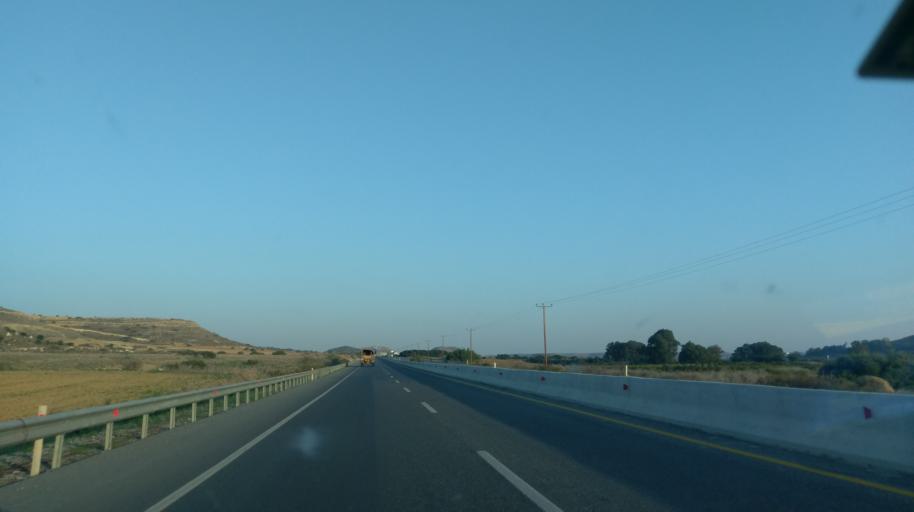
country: CY
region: Lefkosia
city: Akaki
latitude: 35.1958
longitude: 33.0989
